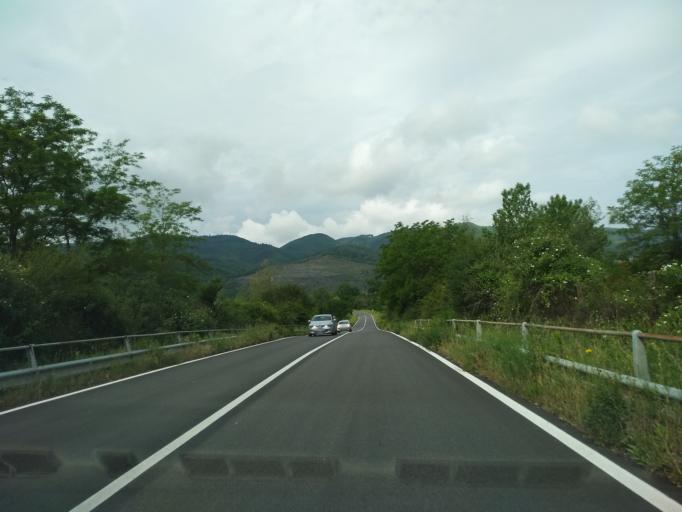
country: IT
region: Tuscany
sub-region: Province of Arezzo
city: Castelnuovo dei Sabbioni
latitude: 43.5608
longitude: 11.4584
